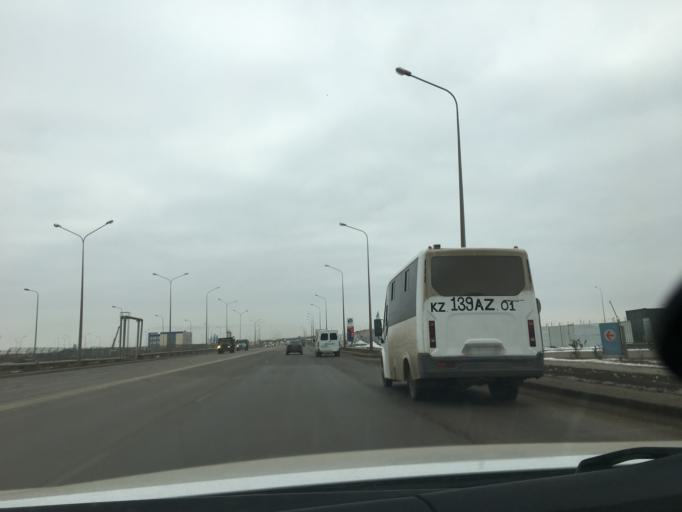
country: KZ
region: Astana Qalasy
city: Astana
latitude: 51.1578
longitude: 71.5254
